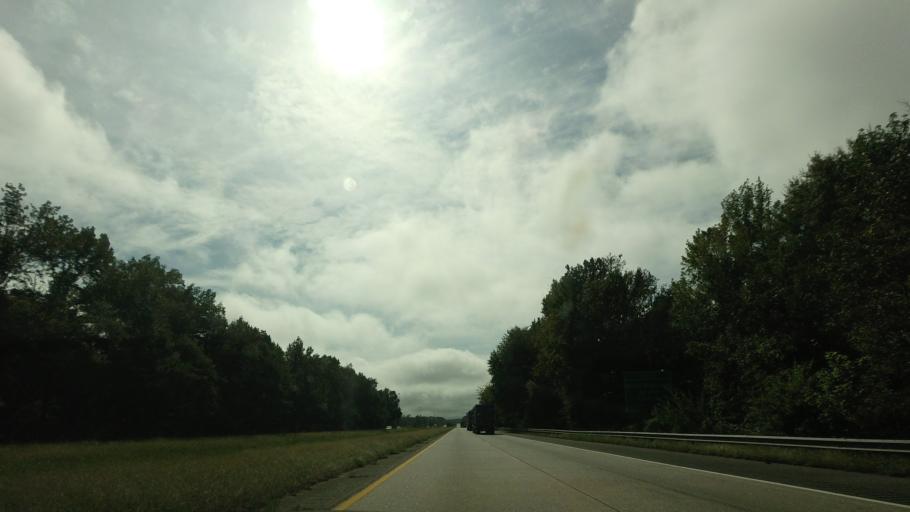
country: US
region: Georgia
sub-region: Bibb County
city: Macon
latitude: 32.8077
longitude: -83.5750
